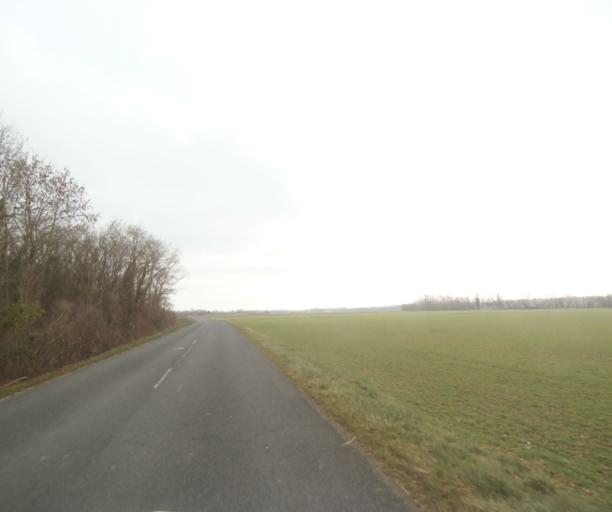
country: FR
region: Champagne-Ardenne
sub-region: Departement de la Haute-Marne
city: Villiers-en-Lieu
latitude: 48.6536
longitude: 4.7906
